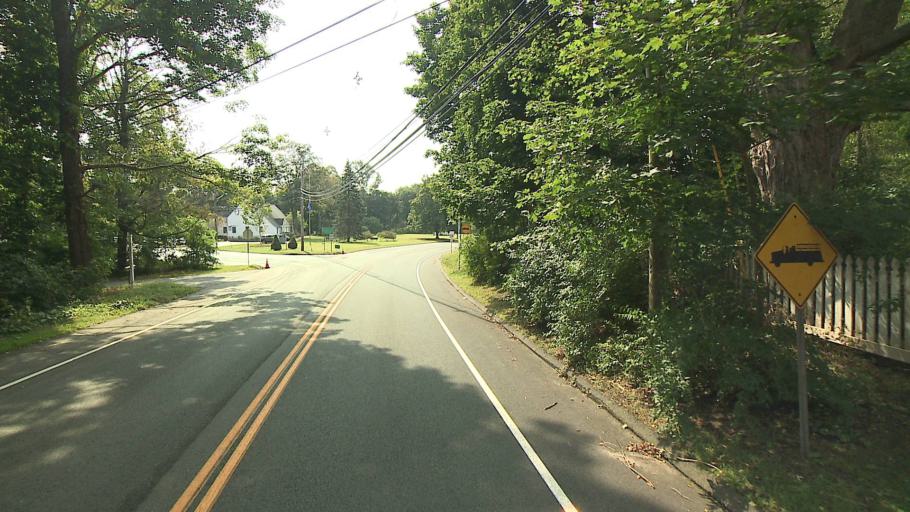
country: US
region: Connecticut
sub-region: Fairfield County
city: Bethel
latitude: 41.3064
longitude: -73.3821
